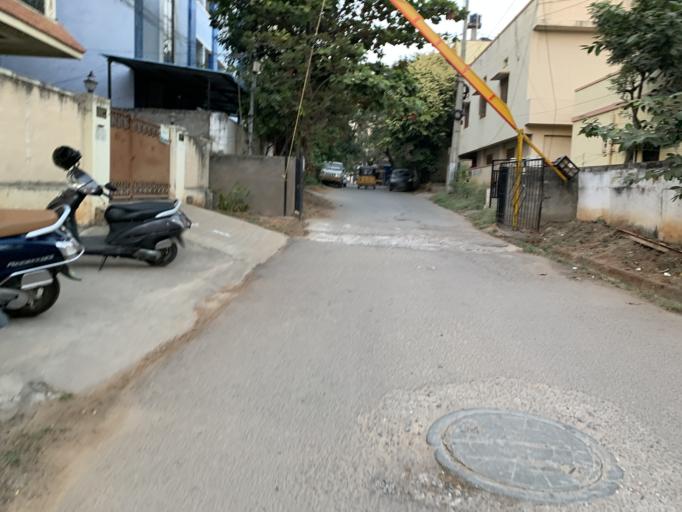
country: IN
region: Telangana
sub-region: Rangareddi
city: Kukatpalli
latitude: 17.4967
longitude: 78.3834
